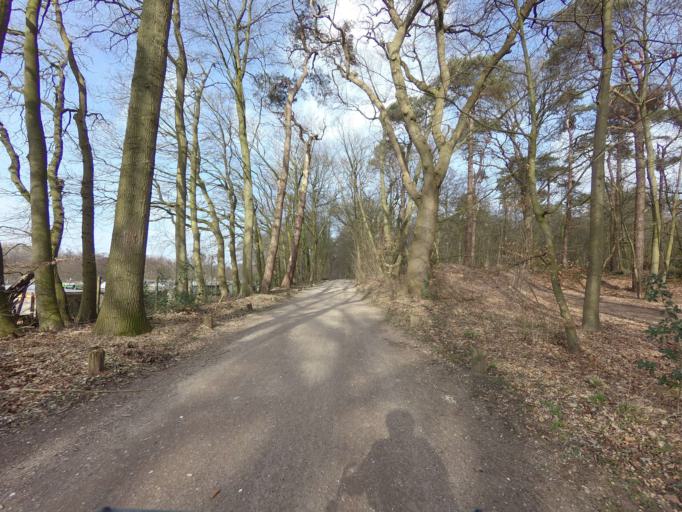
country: NL
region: North Holland
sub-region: Gemeente Bussum
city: Bussum
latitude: 52.2496
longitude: 5.1400
